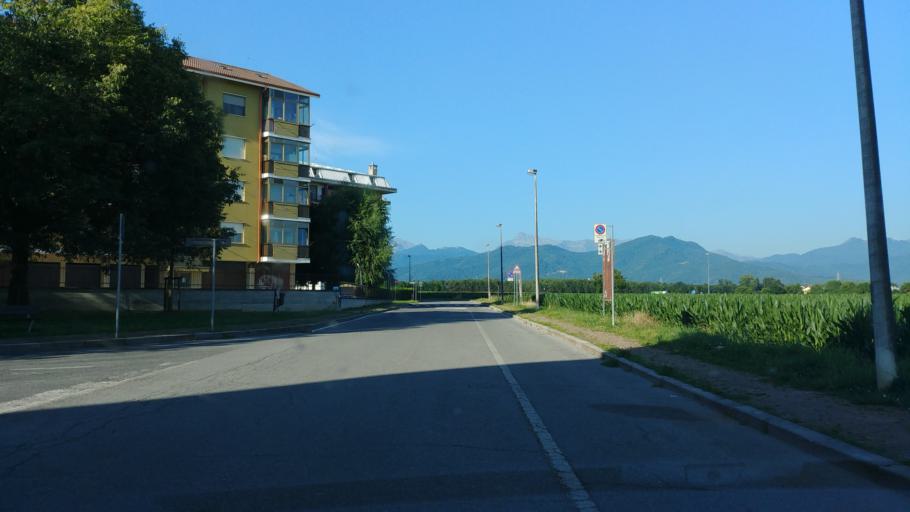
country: IT
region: Piedmont
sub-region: Provincia di Cuneo
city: San Defendente
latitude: 44.3972
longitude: 7.5181
